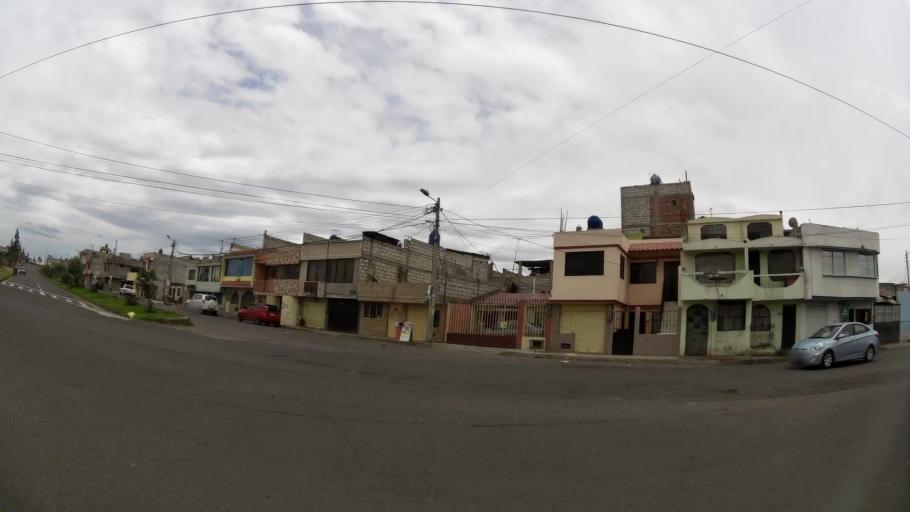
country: EC
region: Cotopaxi
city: San Miguel de Salcedo
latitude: -1.0324
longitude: -78.5897
